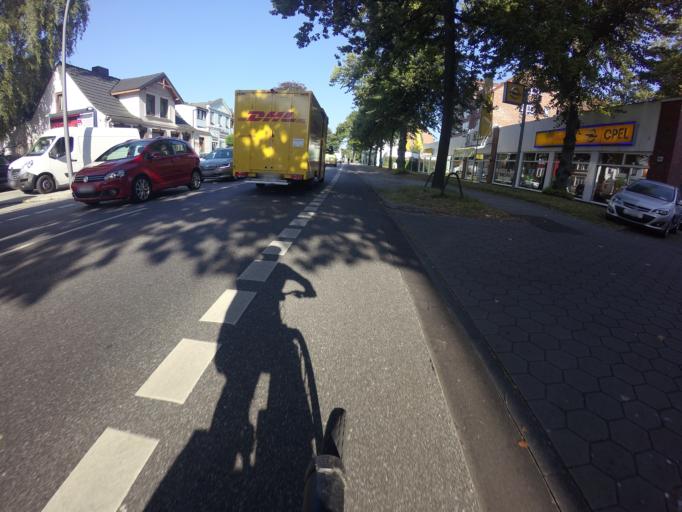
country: DE
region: Hamburg
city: Altona
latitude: 53.5678
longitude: 9.9058
